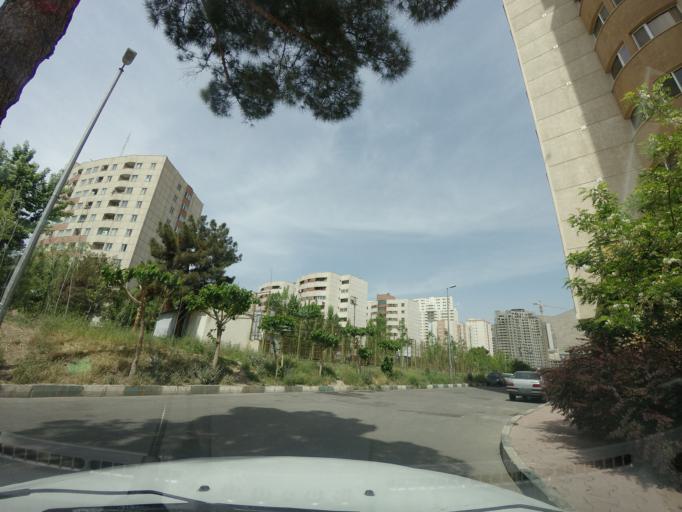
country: IR
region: Tehran
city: Shahr-e Qods
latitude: 35.7454
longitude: 51.1975
